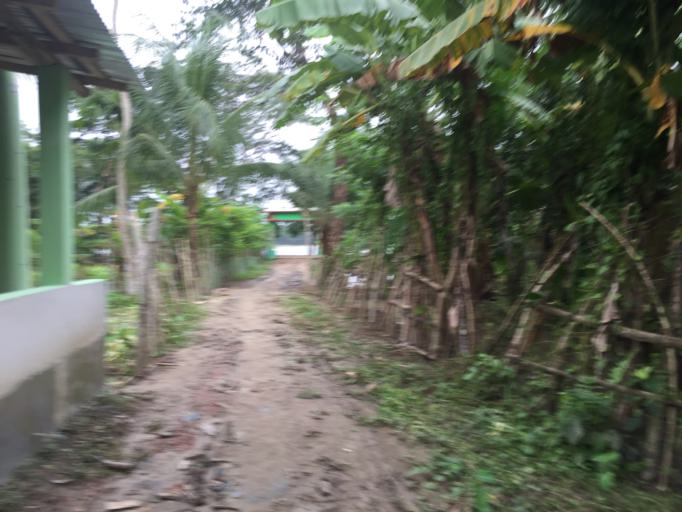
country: BD
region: Barisal
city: Mathba
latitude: 22.1908
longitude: 89.9296
